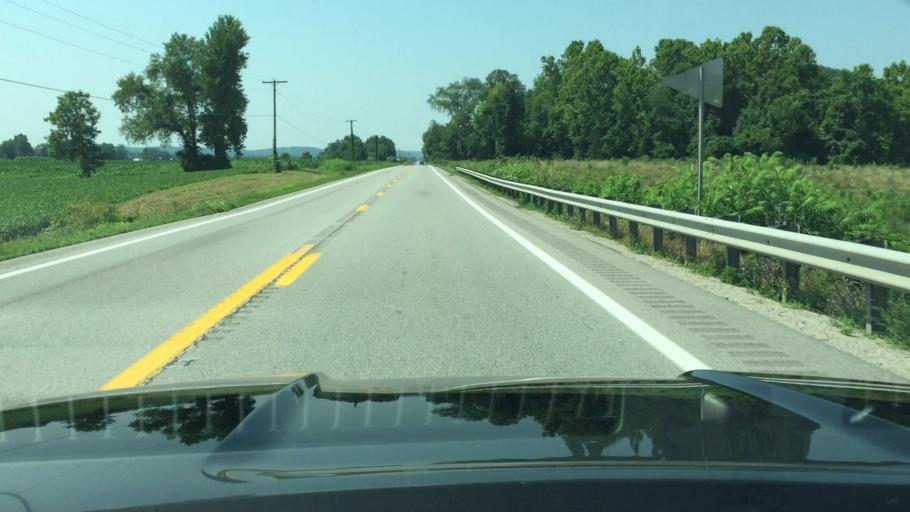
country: US
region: West Virginia
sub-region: Putnam County
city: Buffalo
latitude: 38.6803
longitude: -81.9649
